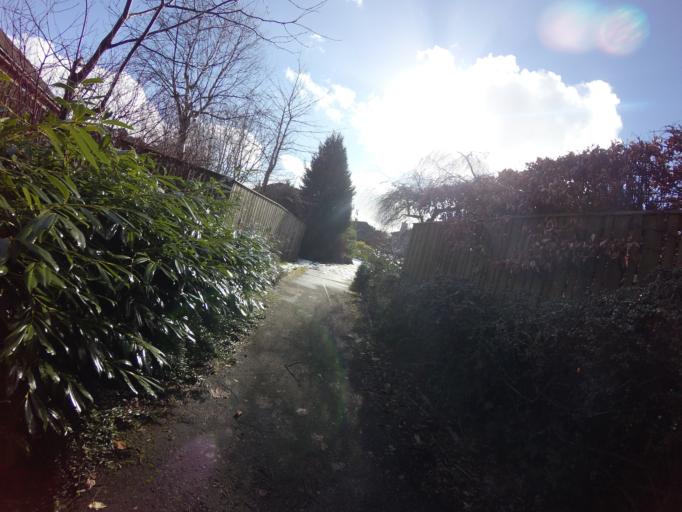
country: GB
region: Scotland
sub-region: West Lothian
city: Livingston
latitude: 55.8630
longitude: -3.5164
